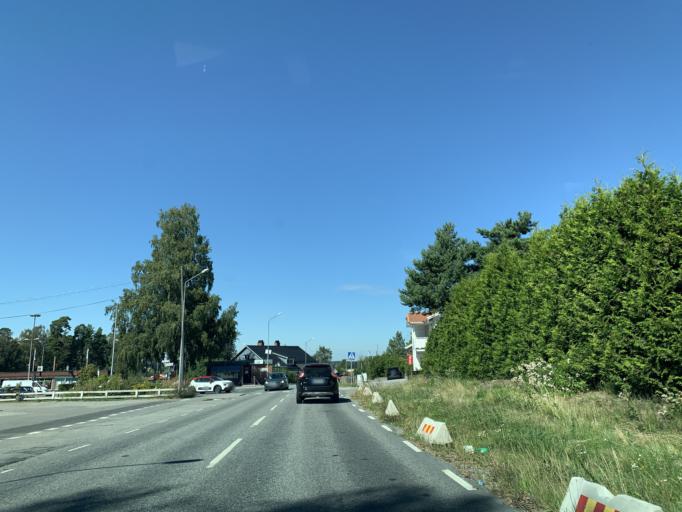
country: SE
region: Stockholm
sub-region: Ekero Kommun
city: Ekeroe
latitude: 59.2747
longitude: 17.7860
